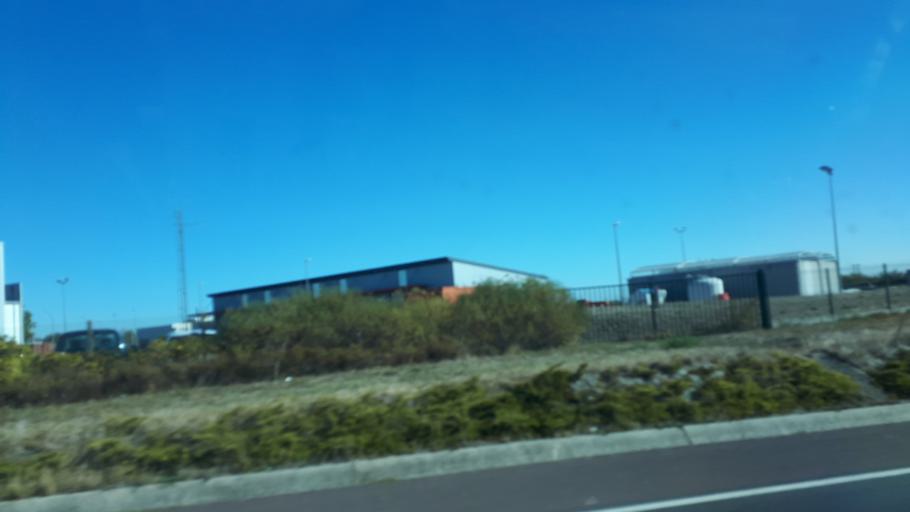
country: FR
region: Centre
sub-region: Departement d'Eure-et-Loir
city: Chateaudun
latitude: 48.0608
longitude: 1.3351
